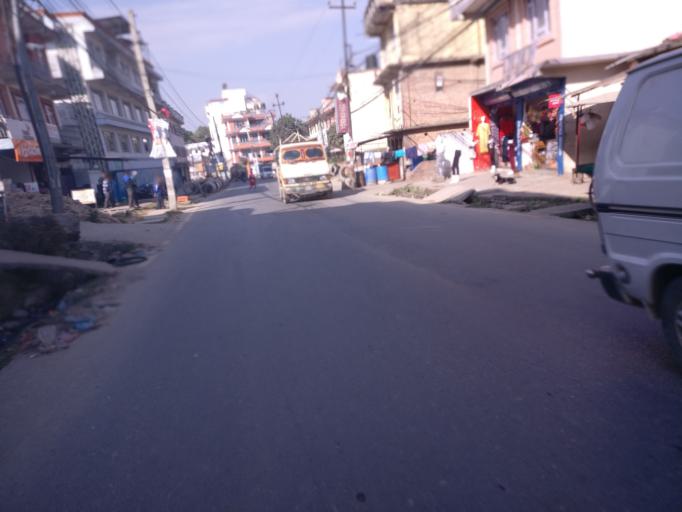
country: NP
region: Central Region
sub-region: Bagmati Zone
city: Patan
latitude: 27.6509
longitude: 85.3055
